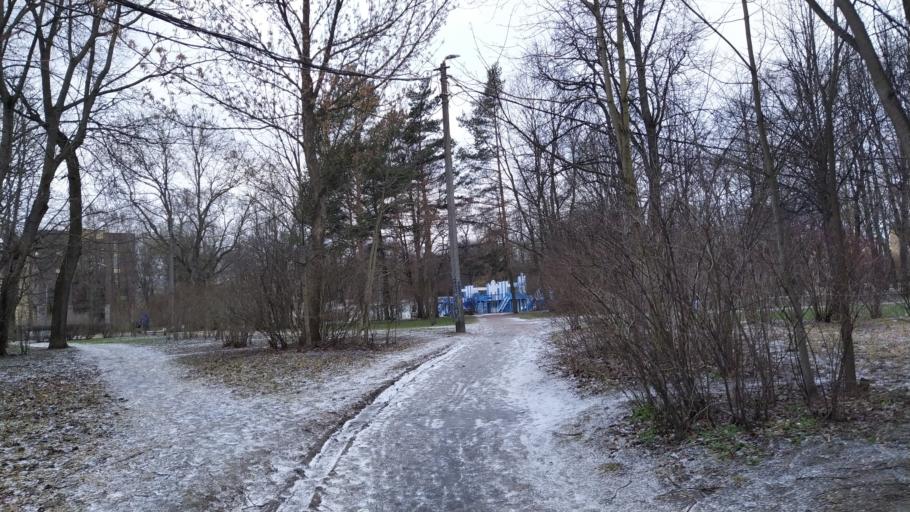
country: RU
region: St.-Petersburg
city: Pushkin
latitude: 59.7220
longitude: 30.4256
